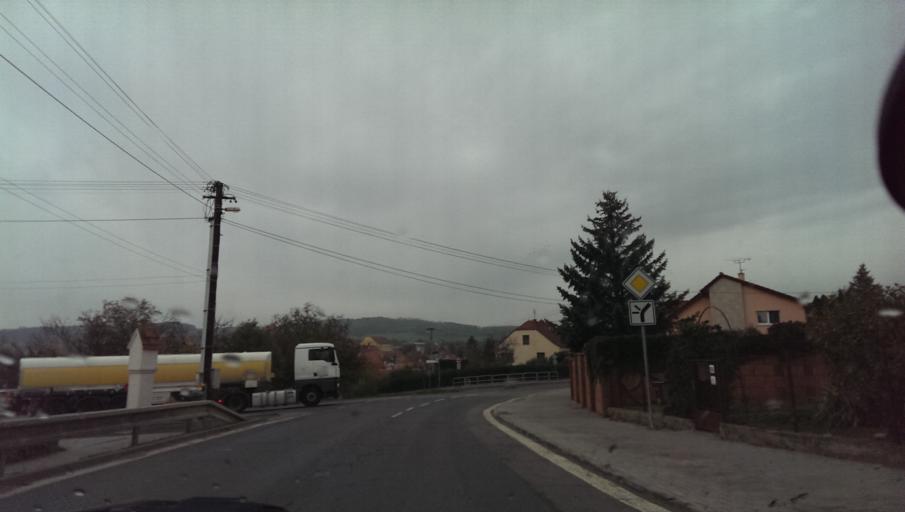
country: CZ
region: South Moravian
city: Moravany
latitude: 49.1478
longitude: 16.5806
